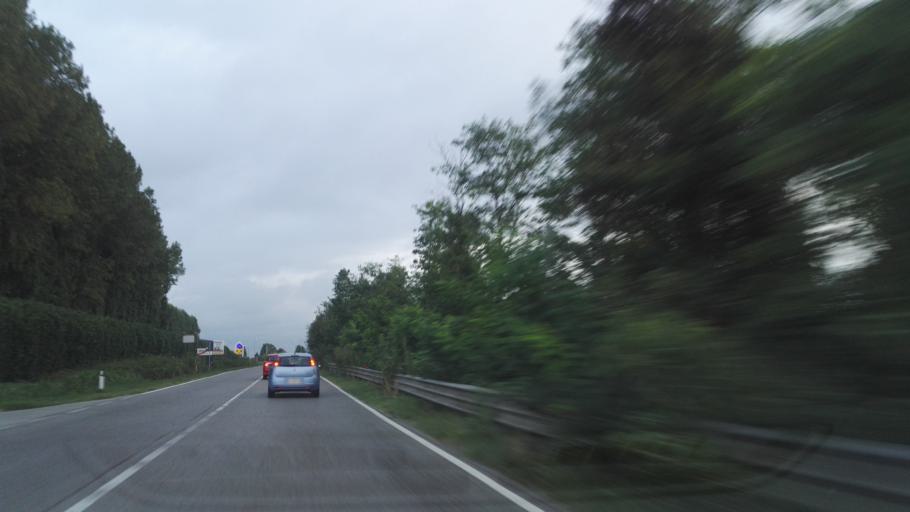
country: IT
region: Lombardy
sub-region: Citta metropolitana di Milano
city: Caleppio
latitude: 45.4400
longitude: 9.3847
